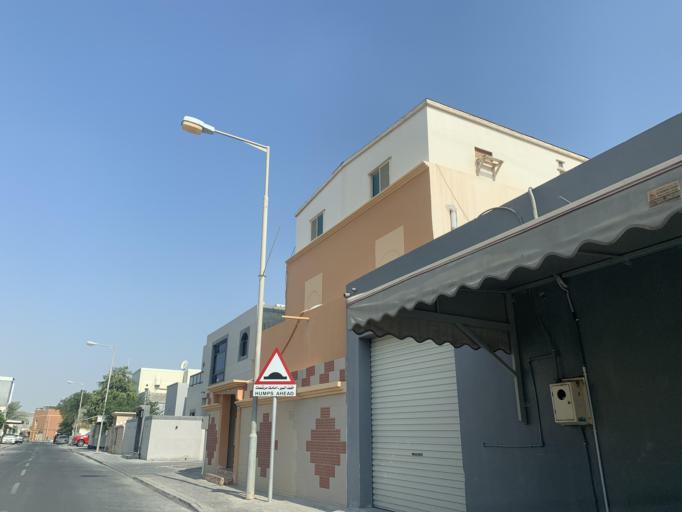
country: BH
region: Central Governorate
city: Madinat Hamad
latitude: 26.1212
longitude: 50.4926
